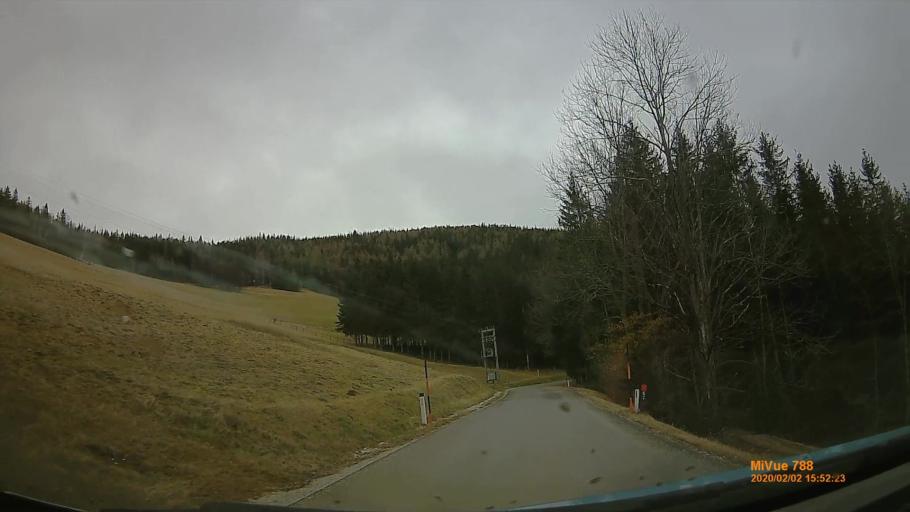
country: AT
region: Lower Austria
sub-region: Politischer Bezirk Neunkirchen
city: Reichenau an der Rax
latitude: 47.6772
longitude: 15.8017
